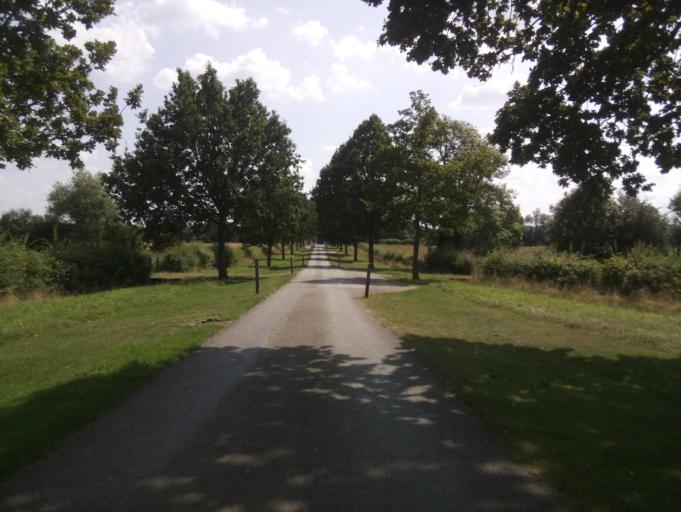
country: GB
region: England
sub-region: Gloucestershire
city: Moreton in Marsh
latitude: 51.9920
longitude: -1.7356
